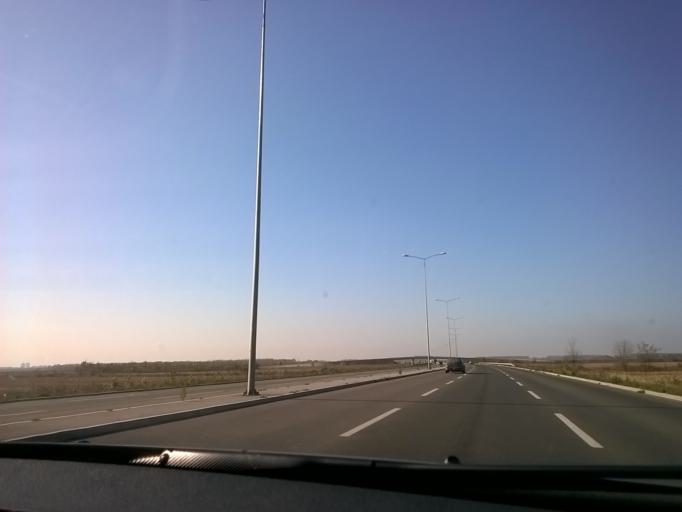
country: RS
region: Central Serbia
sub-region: Belgrade
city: Zemun
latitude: 44.8986
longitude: 20.4246
